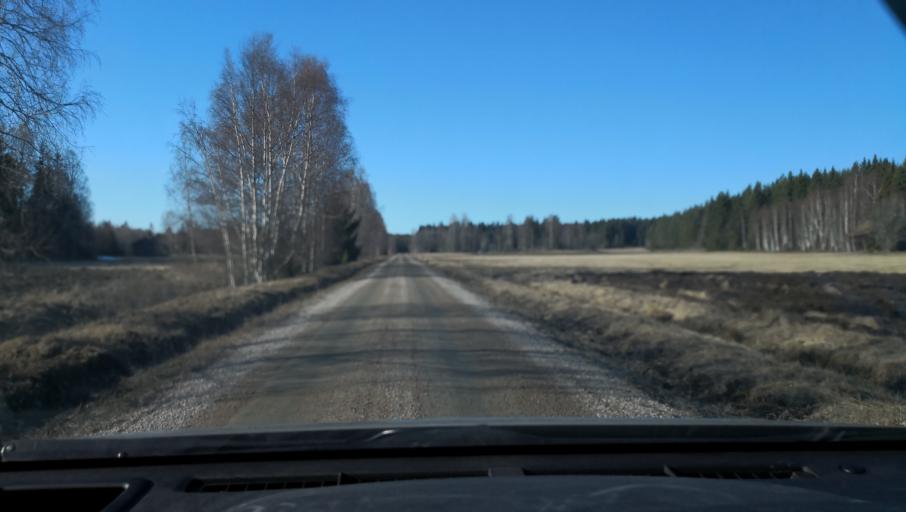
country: SE
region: Vaestmanland
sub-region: Sala Kommun
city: Sala
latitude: 60.1291
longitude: 16.6535
